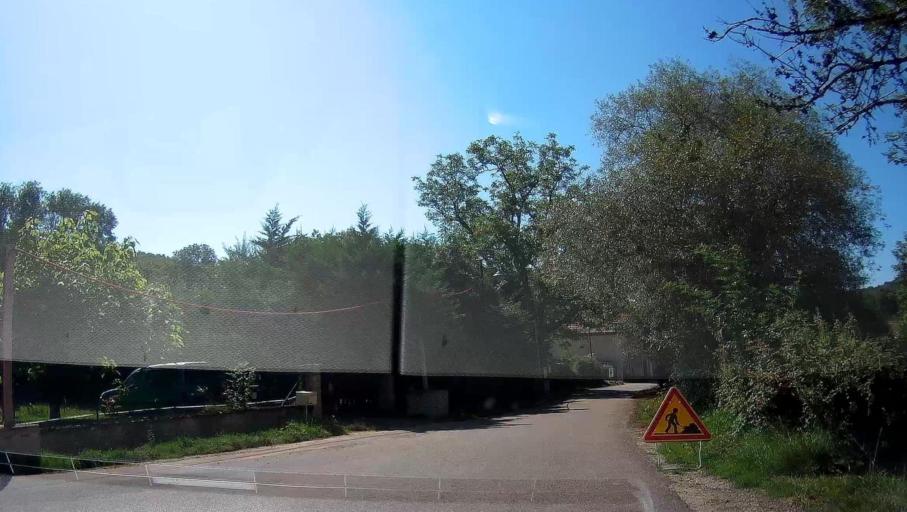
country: FR
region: Bourgogne
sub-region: Departement de la Cote-d'Or
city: Nolay
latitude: 46.9781
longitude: 4.6449
